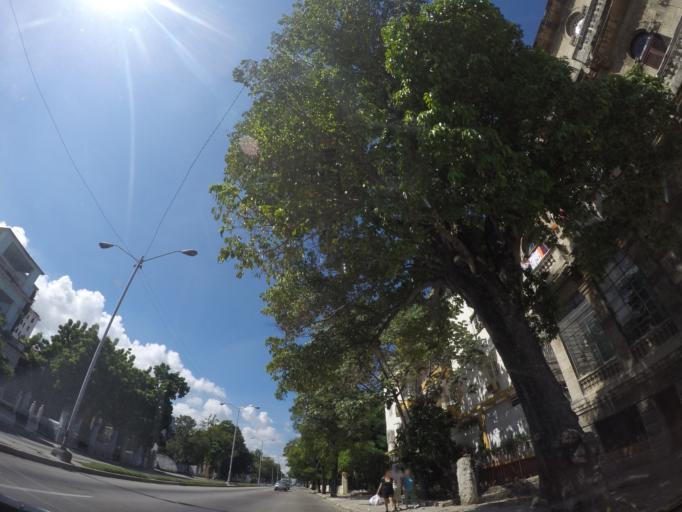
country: CU
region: La Habana
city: Regla
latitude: 23.0996
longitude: -82.3195
